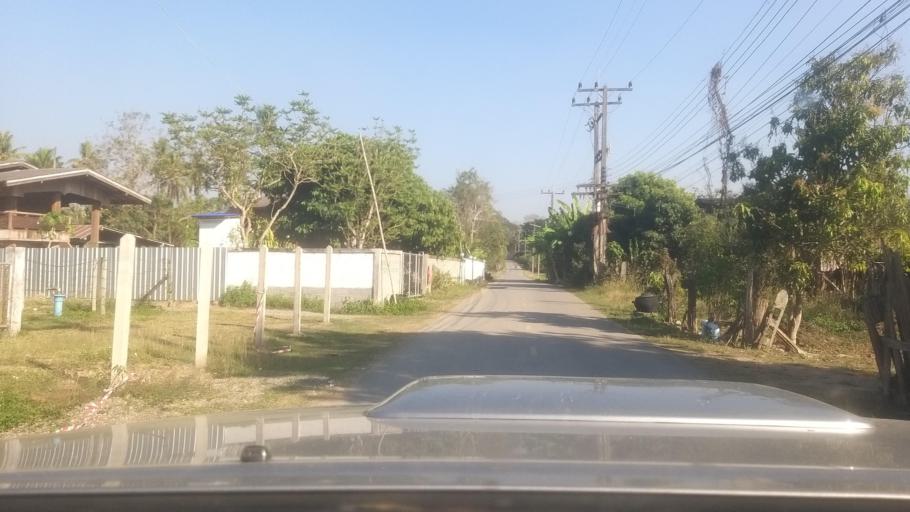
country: TH
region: Phrae
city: Phrae
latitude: 18.2617
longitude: 99.9953
